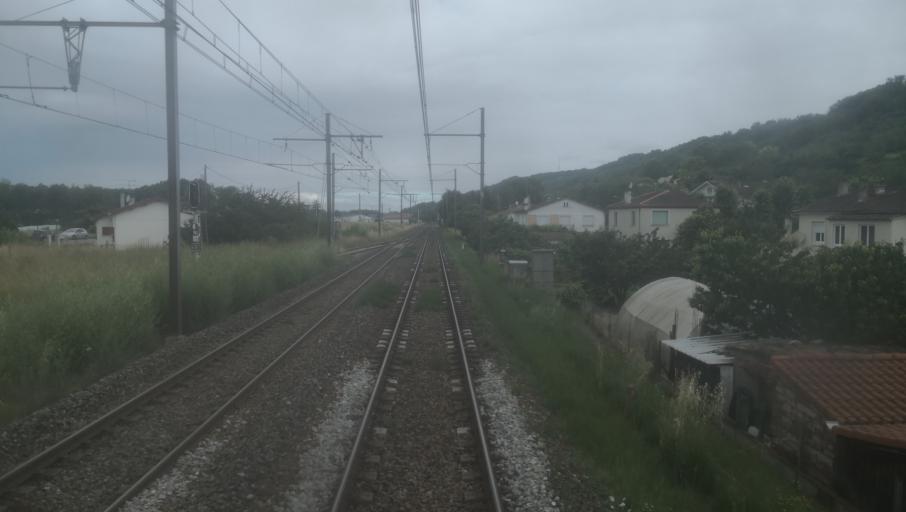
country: FR
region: Aquitaine
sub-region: Departement du Lot-et-Garonne
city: Port-Sainte-Marie
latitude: 44.2521
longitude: 0.3822
